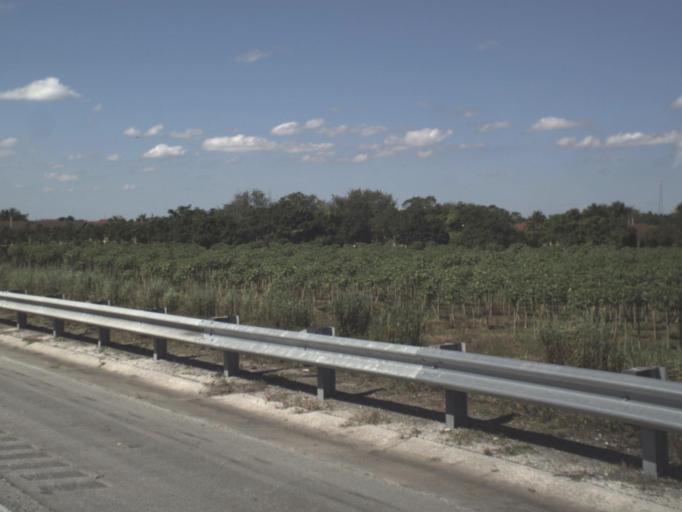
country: US
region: Florida
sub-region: Miami-Dade County
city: Homestead
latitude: 25.4687
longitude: -80.4535
